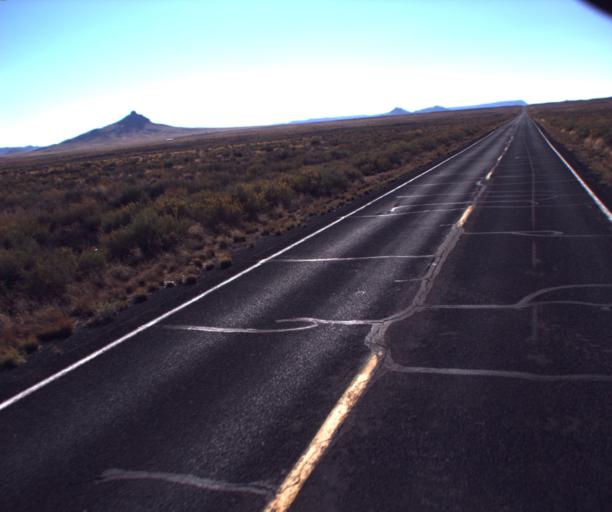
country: US
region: Arizona
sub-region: Navajo County
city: Dilkon
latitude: 35.5754
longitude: -110.4619
